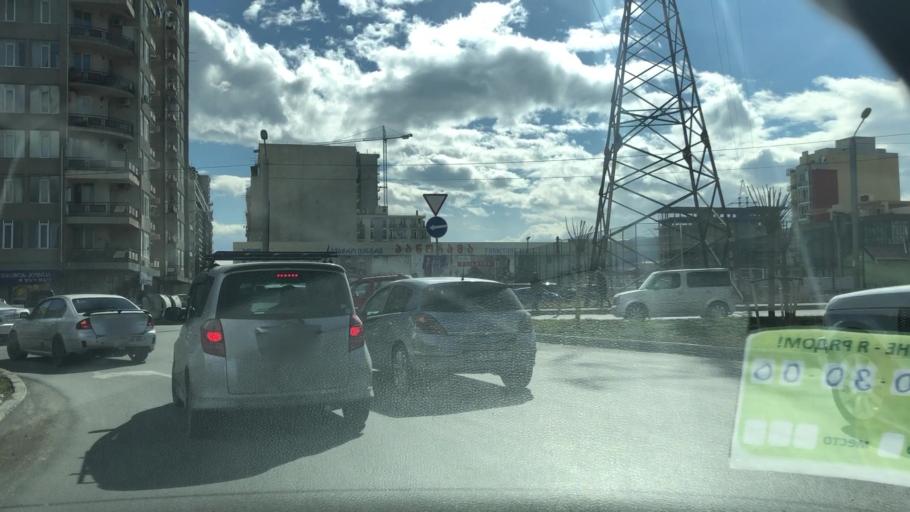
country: GE
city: Zahesi
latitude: 41.7871
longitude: 44.7653
